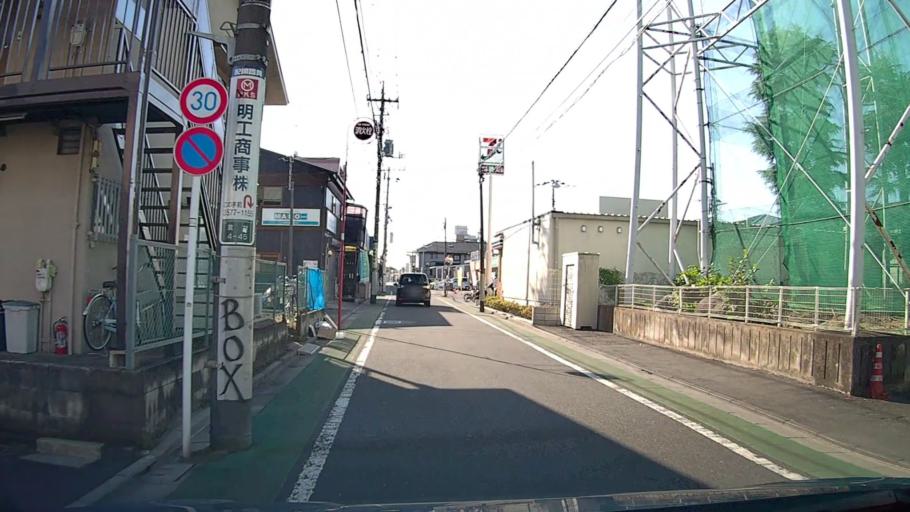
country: JP
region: Saitama
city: Wako
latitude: 35.7441
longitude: 139.6257
